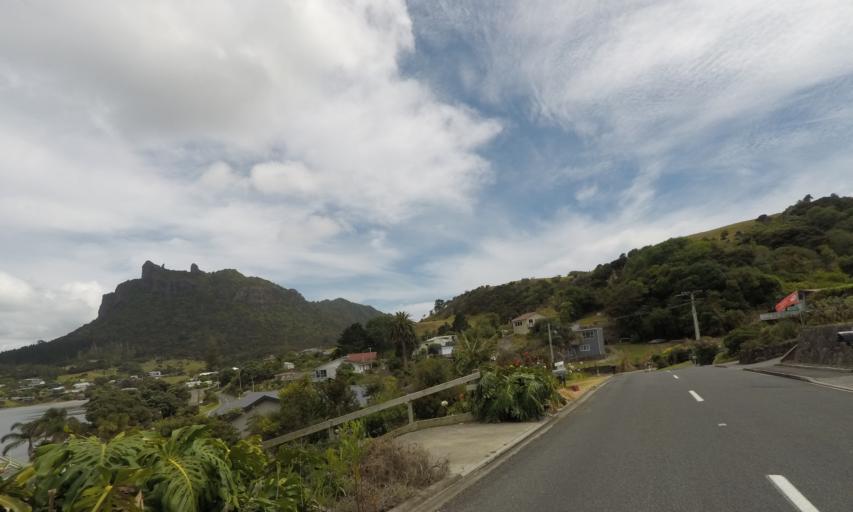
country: NZ
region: Northland
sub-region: Whangarei
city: Ruakaka
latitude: -35.8290
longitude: 174.5302
